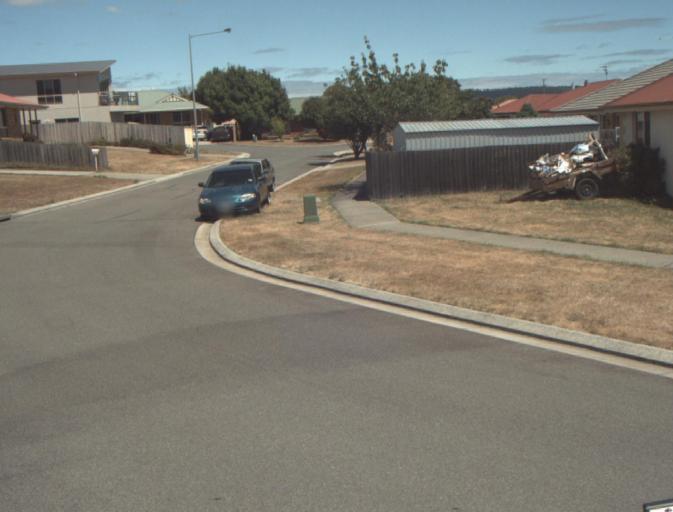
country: AU
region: Tasmania
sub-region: Launceston
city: Mayfield
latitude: -41.3857
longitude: 147.1166
